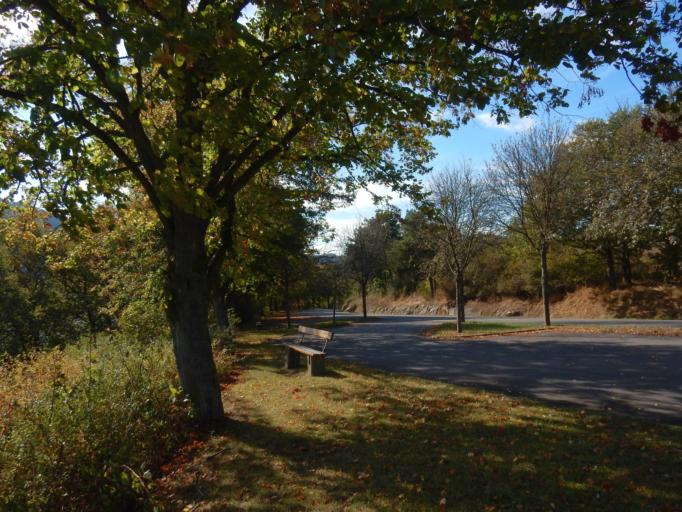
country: LU
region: Diekirch
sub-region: Canton de Wiltz
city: Bavigne
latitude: 49.9055
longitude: 5.8785
